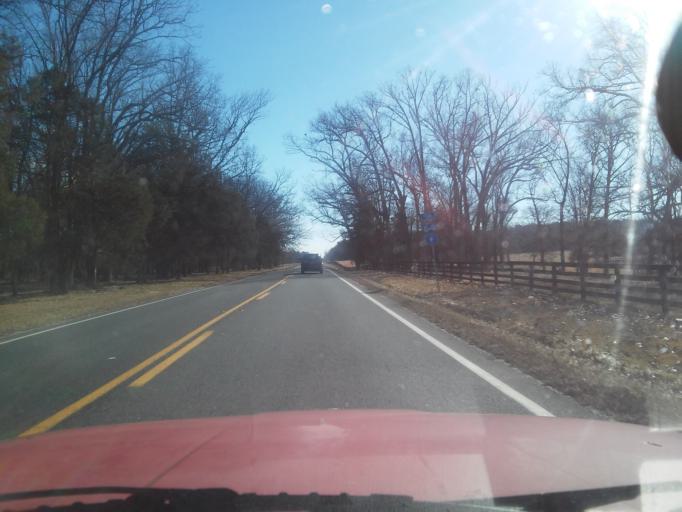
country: US
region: Virginia
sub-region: Orange County
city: Gordonsville
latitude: 38.0140
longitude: -78.1913
